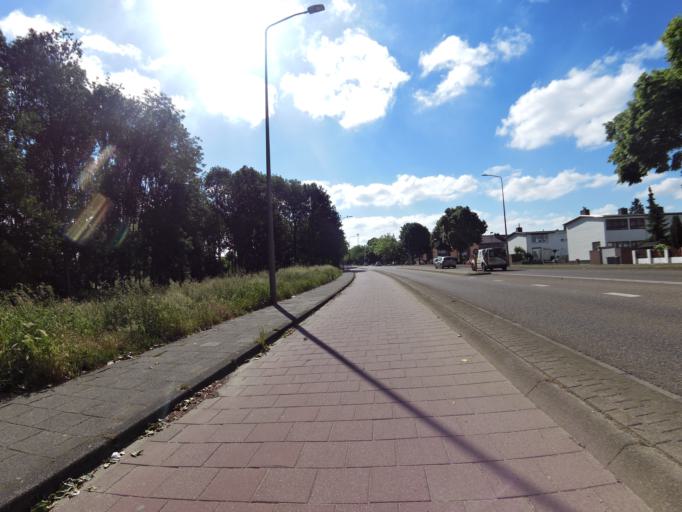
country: NL
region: Limburg
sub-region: Gemeente Heerlen
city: Heerlen
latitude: 50.9000
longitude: 5.9744
